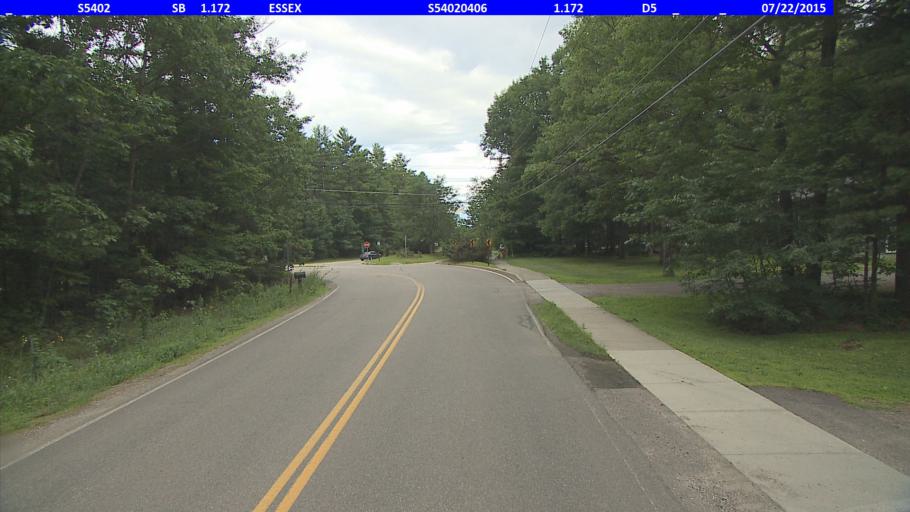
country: US
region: Vermont
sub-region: Chittenden County
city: Jericho
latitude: 44.4952
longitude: -73.0497
